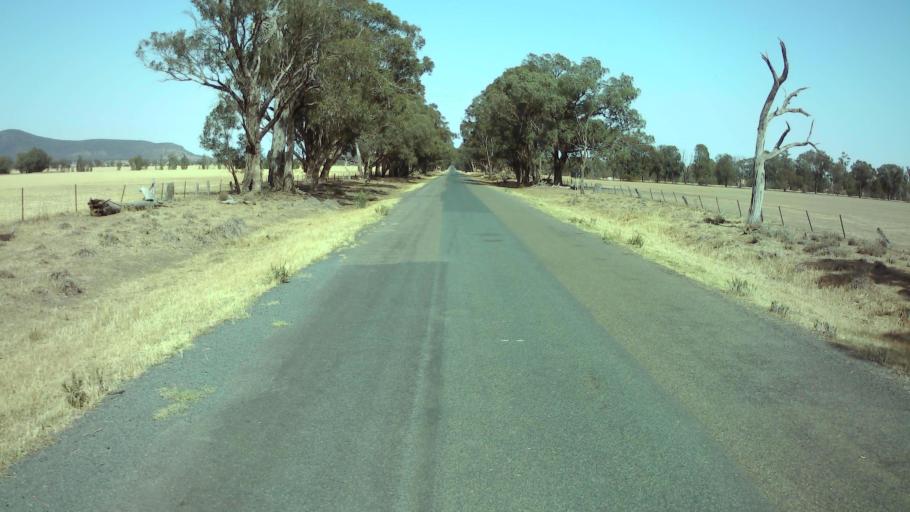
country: AU
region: New South Wales
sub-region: Weddin
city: Grenfell
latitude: -33.8662
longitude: 148.0537
